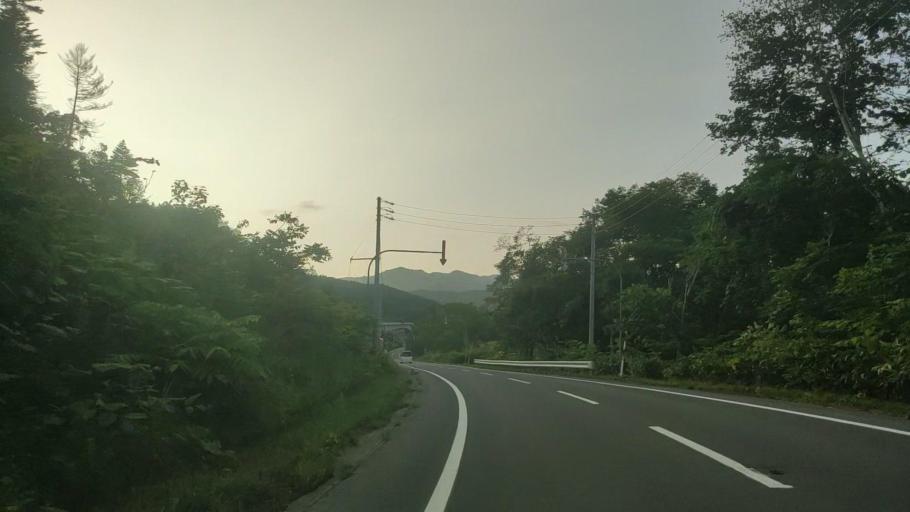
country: JP
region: Hokkaido
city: Bibai
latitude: 43.2237
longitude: 142.0480
